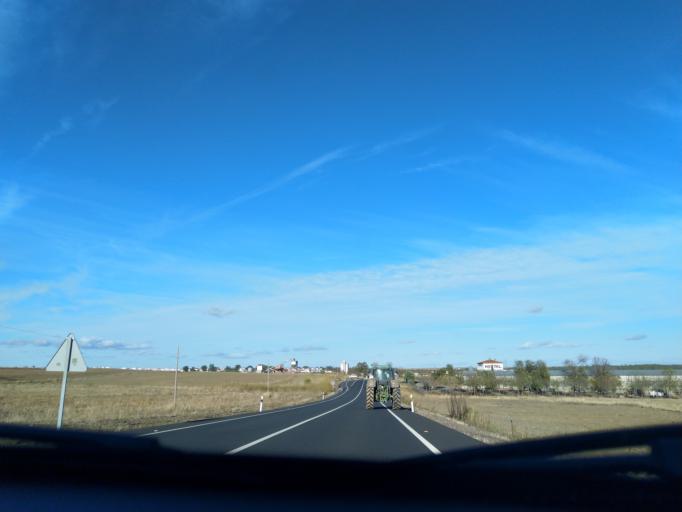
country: ES
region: Extremadura
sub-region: Provincia de Badajoz
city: Ahillones
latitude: 38.2705
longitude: -5.8359
